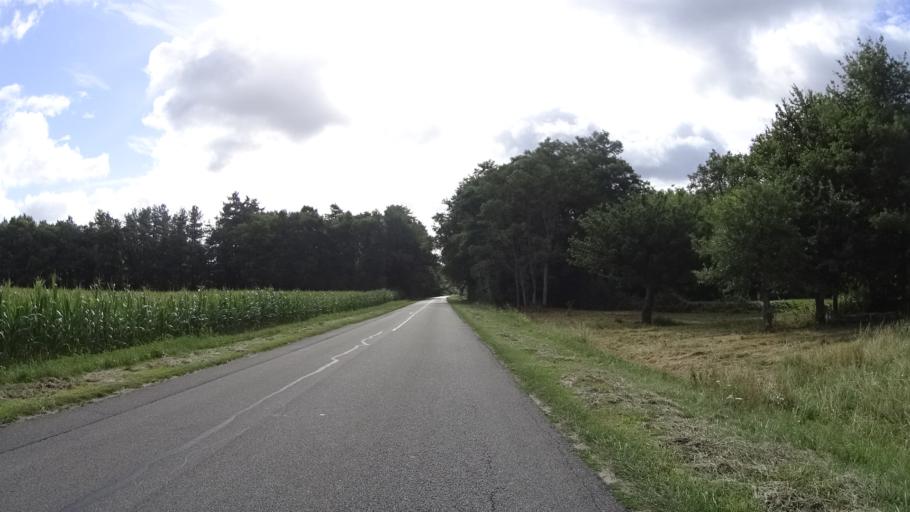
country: FR
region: Centre
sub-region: Departement du Loiret
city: Lorris
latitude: 47.8933
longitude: 2.4832
